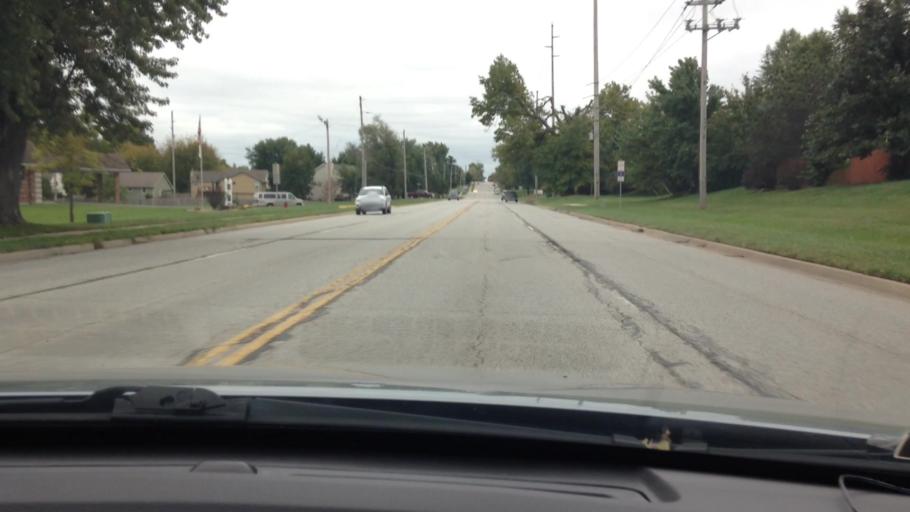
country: US
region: Kansas
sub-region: Leavenworth County
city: Leavenworth
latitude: 39.2759
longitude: -94.9279
